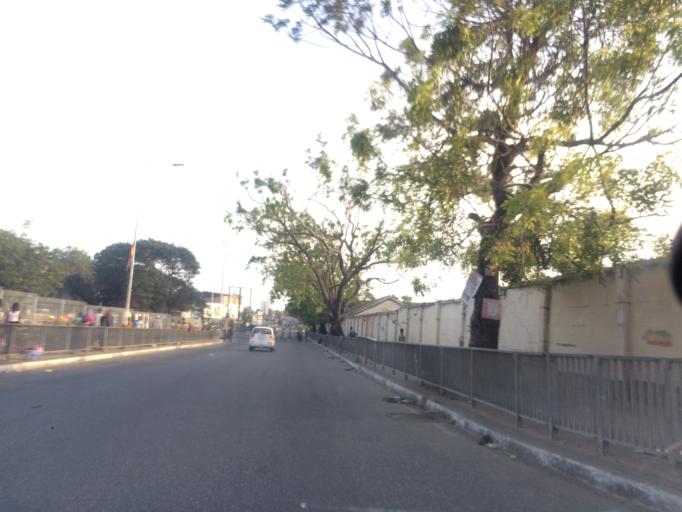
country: GH
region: Greater Accra
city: Accra
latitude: 5.5506
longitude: -0.2041
